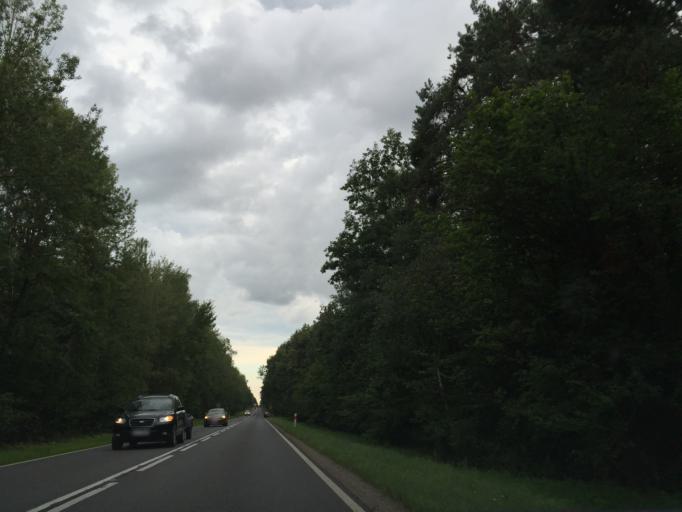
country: PL
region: Lublin Voivodeship
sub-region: Powiat radzynski
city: Borki
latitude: 51.6981
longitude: 22.5076
